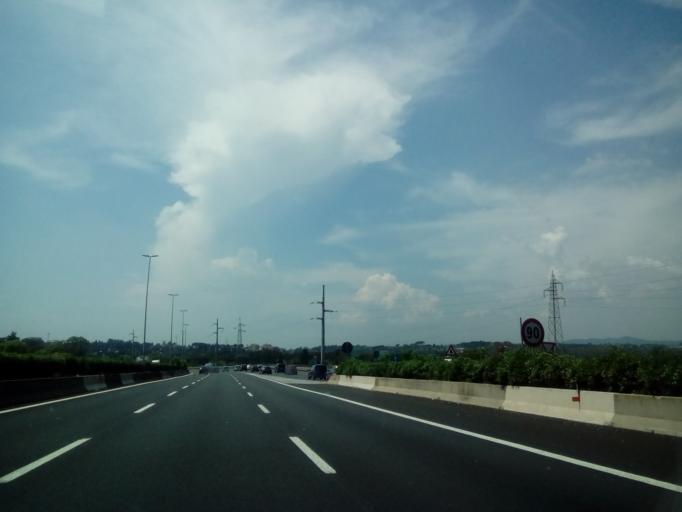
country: IT
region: Latium
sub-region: Citta metropolitana di Roma Capitale
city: Monte Caminetto
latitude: 41.9895
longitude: 12.5120
